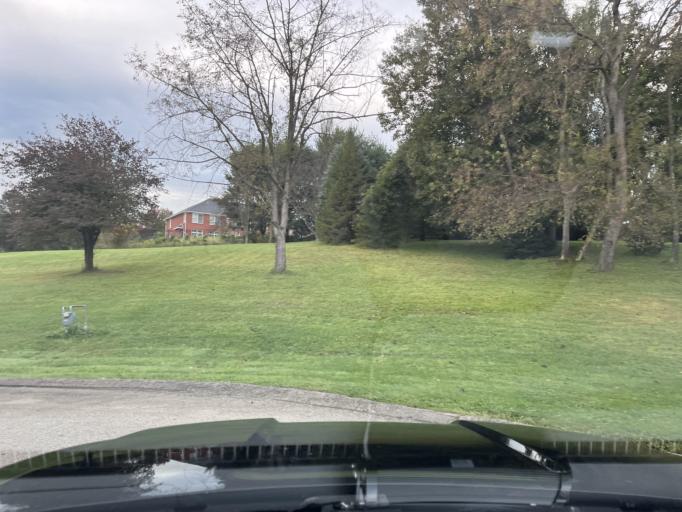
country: US
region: Pennsylvania
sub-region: Fayette County
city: Leith-Hatfield
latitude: 39.8764
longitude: -79.7318
